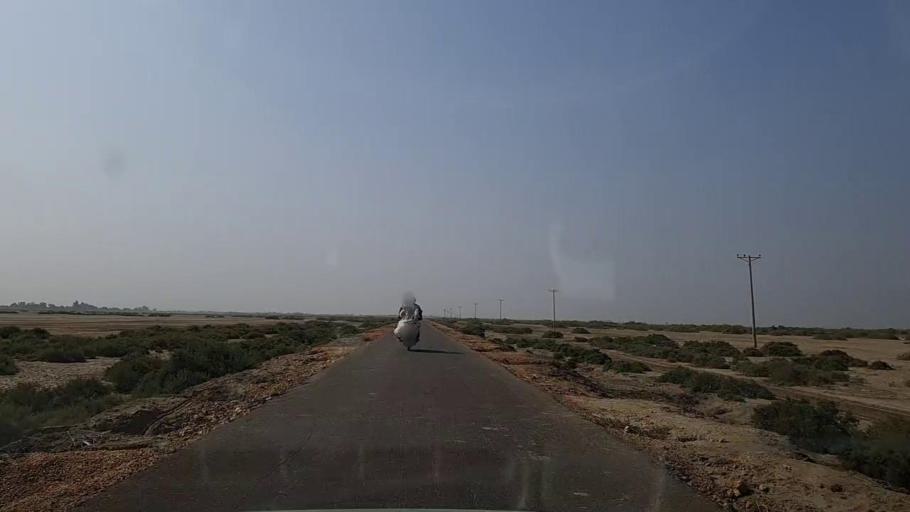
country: PK
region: Sindh
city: Mirpur Sakro
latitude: 24.5289
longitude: 67.5833
